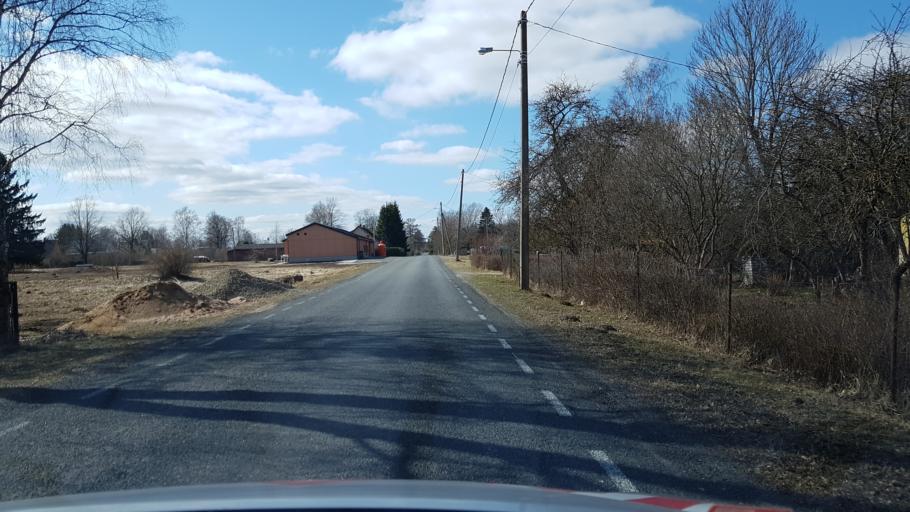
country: EE
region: Laeaene-Virumaa
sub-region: Tapa vald
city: Tapa
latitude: 59.2539
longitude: 25.8296
